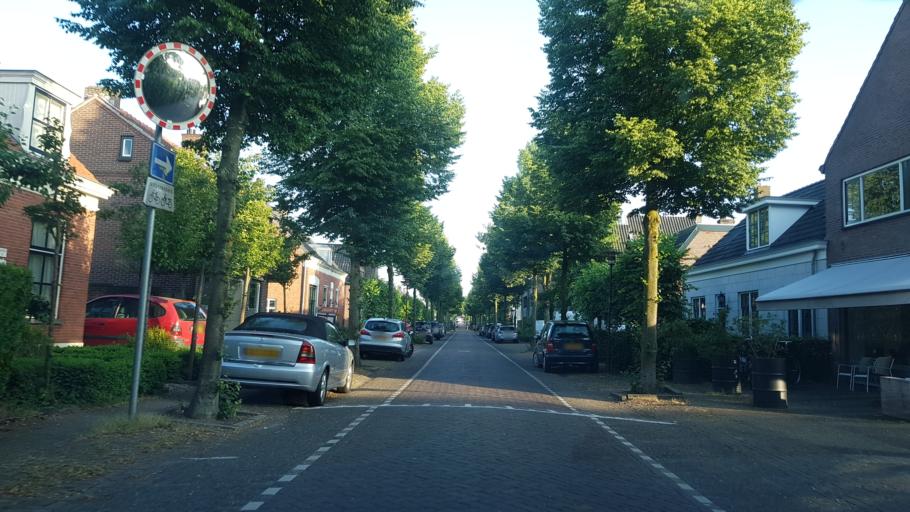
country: NL
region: North Brabant
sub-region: Gemeente Breda
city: Hoge Vucht
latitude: 51.6083
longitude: 4.8172
